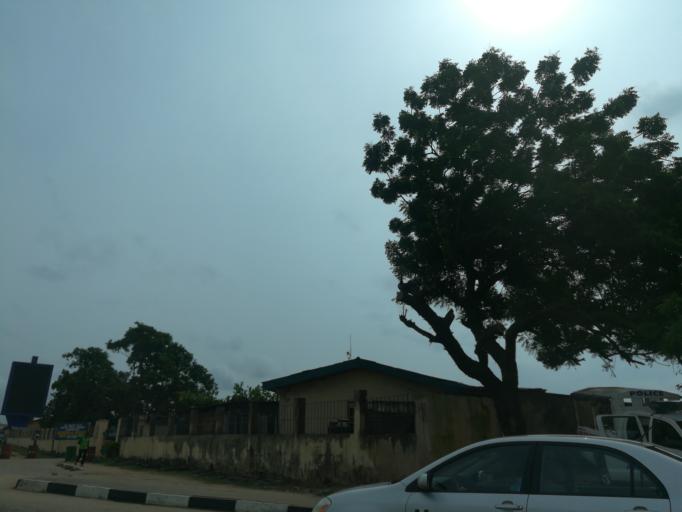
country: NG
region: Lagos
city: Oshodi
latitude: 6.5683
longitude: 3.3311
